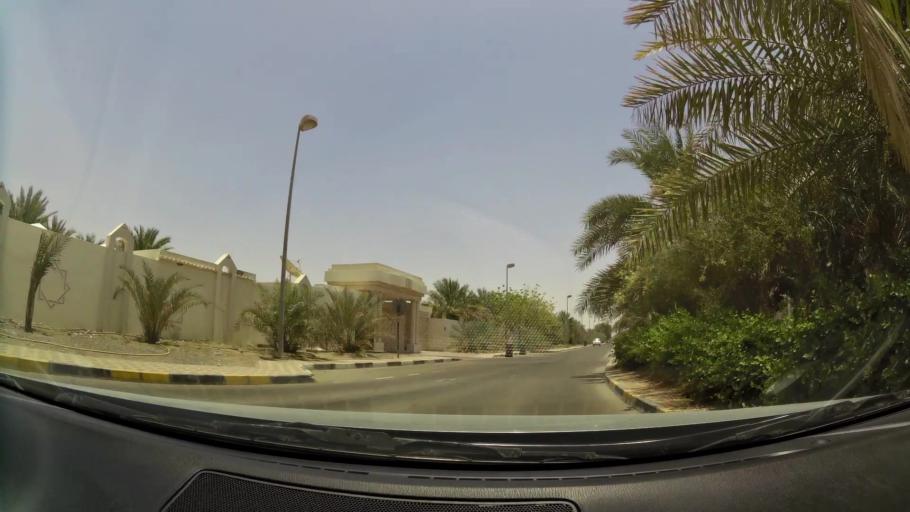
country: OM
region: Al Buraimi
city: Al Buraymi
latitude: 24.2774
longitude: 55.7318
